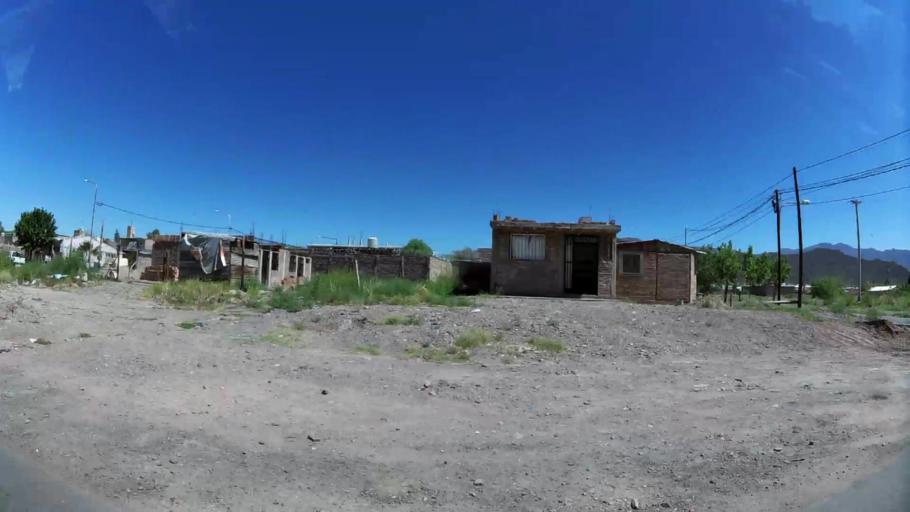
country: AR
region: Mendoza
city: Las Heras
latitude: -32.8410
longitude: -68.8629
